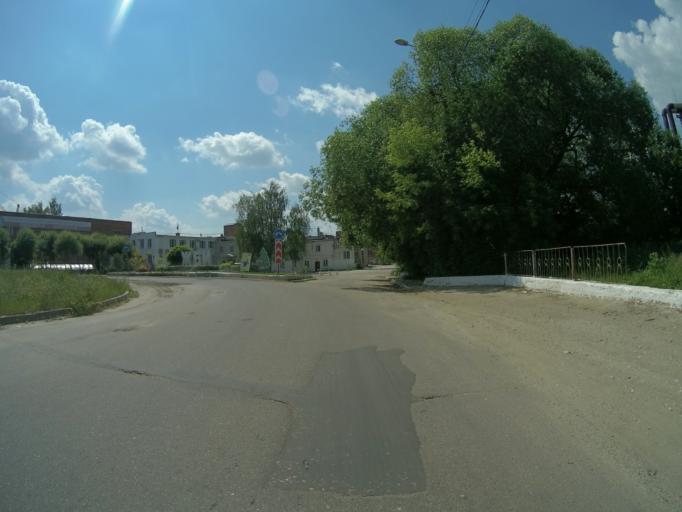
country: RU
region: Vladimir
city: Vladimir
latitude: 56.0991
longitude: 40.3464
